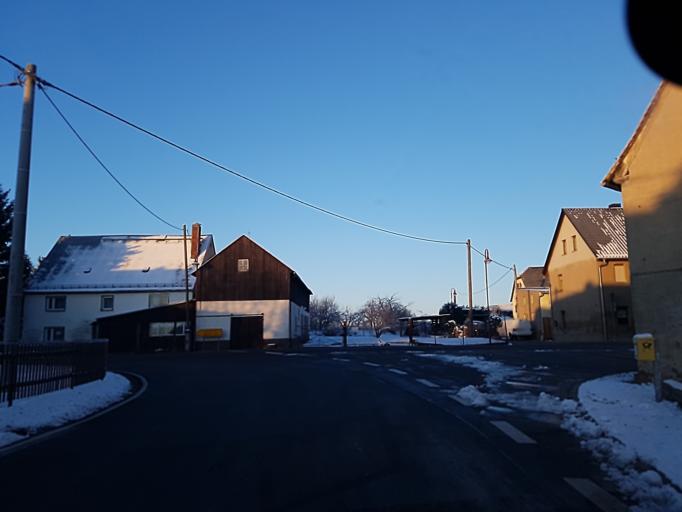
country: DE
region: Saxony
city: Grossweitzschen
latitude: 51.1744
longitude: 13.0432
